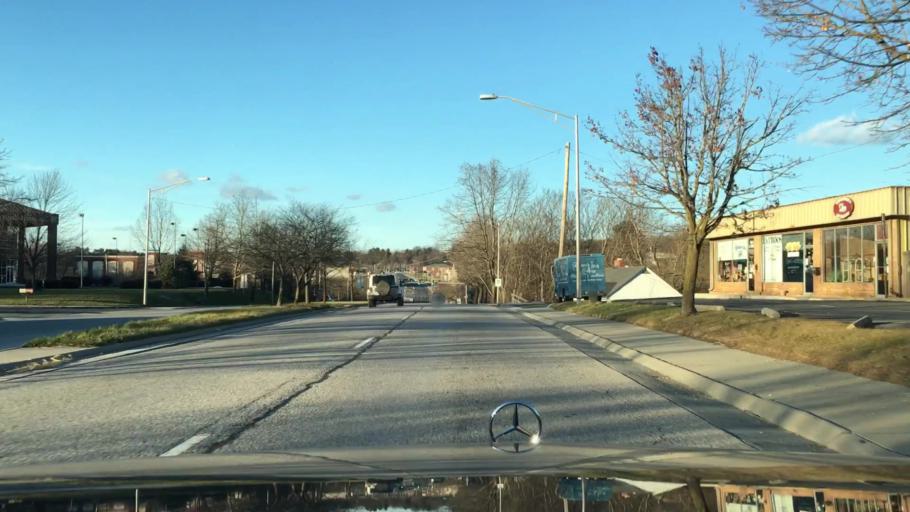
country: US
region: Virginia
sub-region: Montgomery County
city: Blacksburg
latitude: 37.2078
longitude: -80.3989
